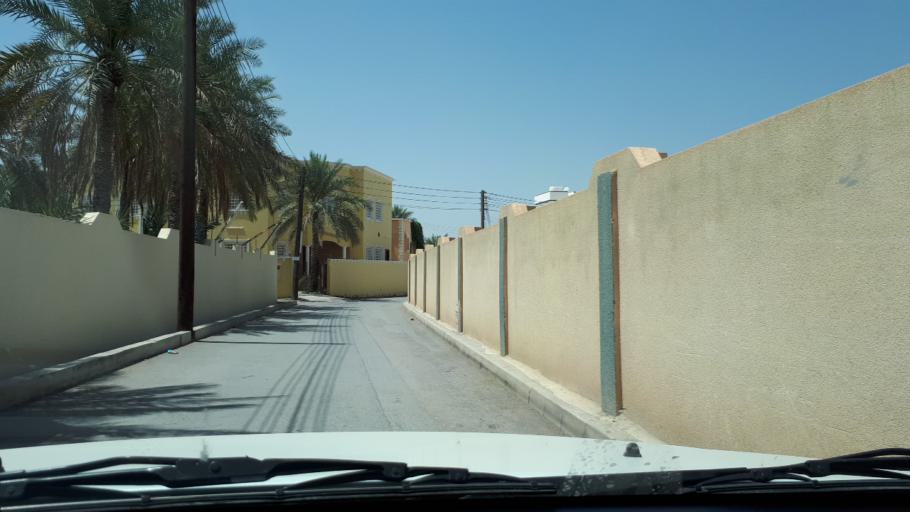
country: OM
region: Muhafazat ad Dakhiliyah
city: Nizwa
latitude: 22.9252
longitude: 57.5303
